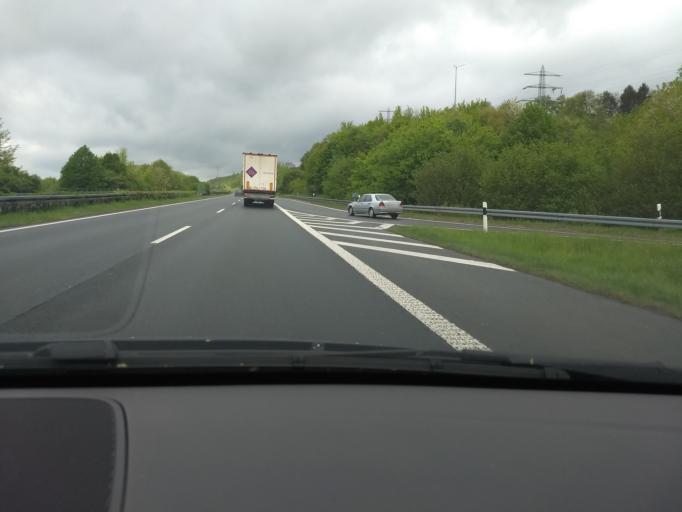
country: DE
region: North Rhine-Westphalia
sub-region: Regierungsbezirk Arnsberg
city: Arnsberg
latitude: 51.4047
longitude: 8.0864
